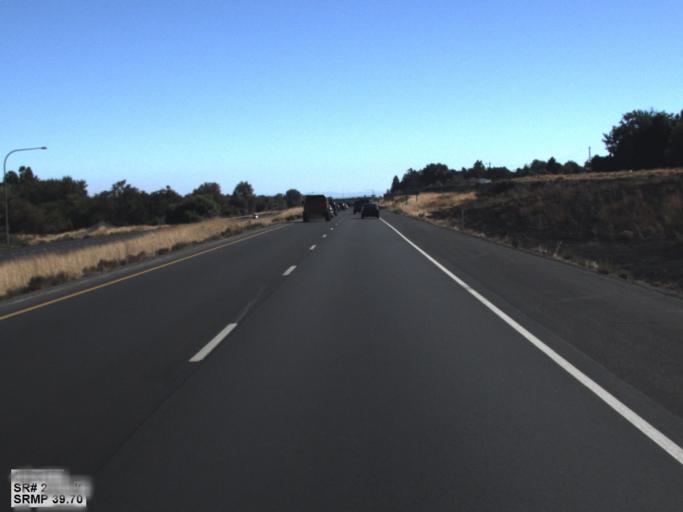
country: US
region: Washington
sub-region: Franklin County
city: West Pasco
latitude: 46.2312
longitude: -119.2070
